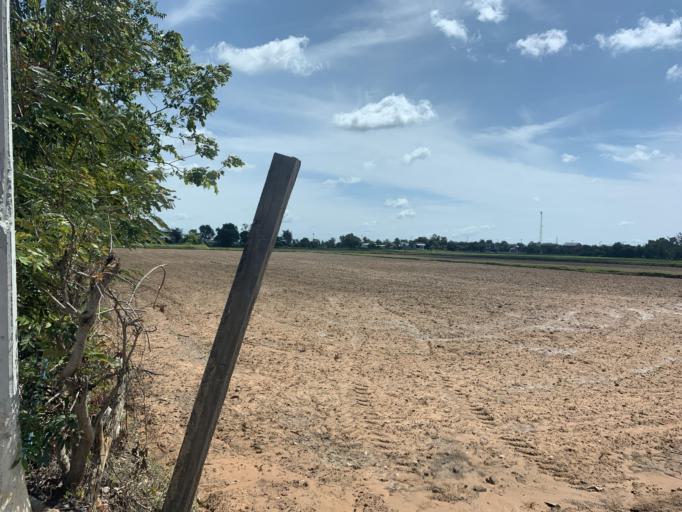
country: TH
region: Surin
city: Tha Tum
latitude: 15.3980
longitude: 103.7580
